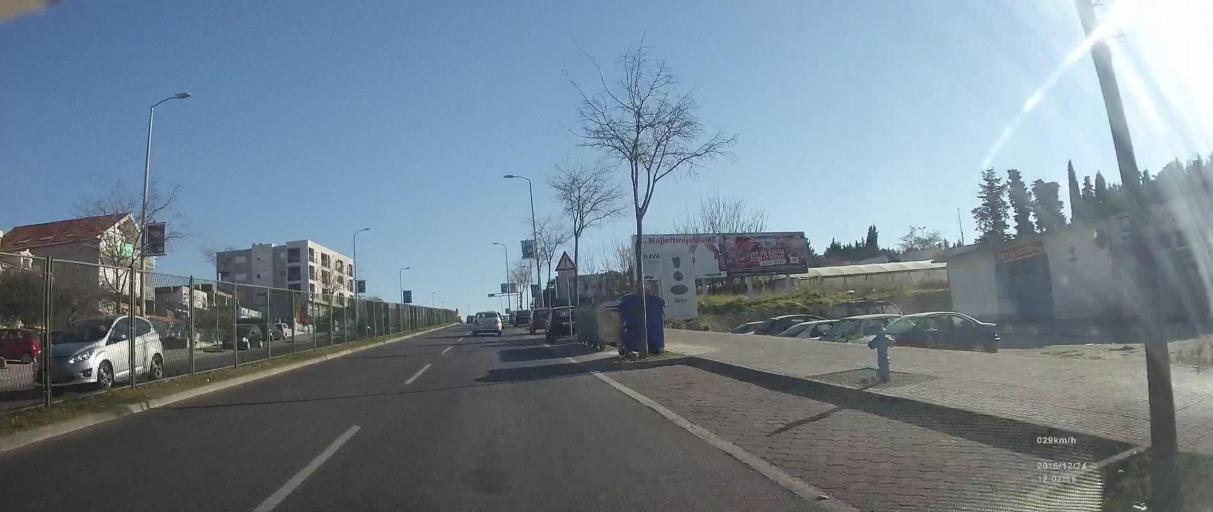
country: HR
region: Splitsko-Dalmatinska
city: Kamen
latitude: 43.5156
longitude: 16.4908
